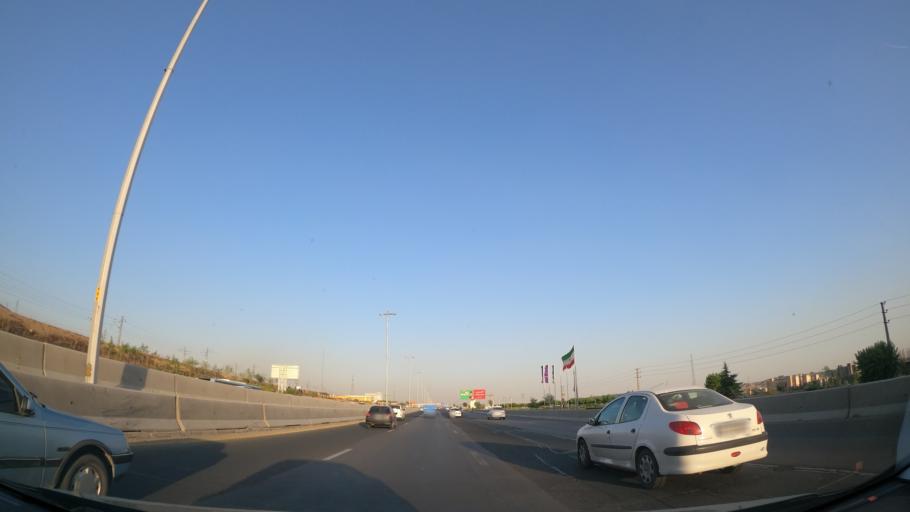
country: IR
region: Tehran
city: Shahr-e Qods
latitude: 35.7550
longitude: 51.0732
